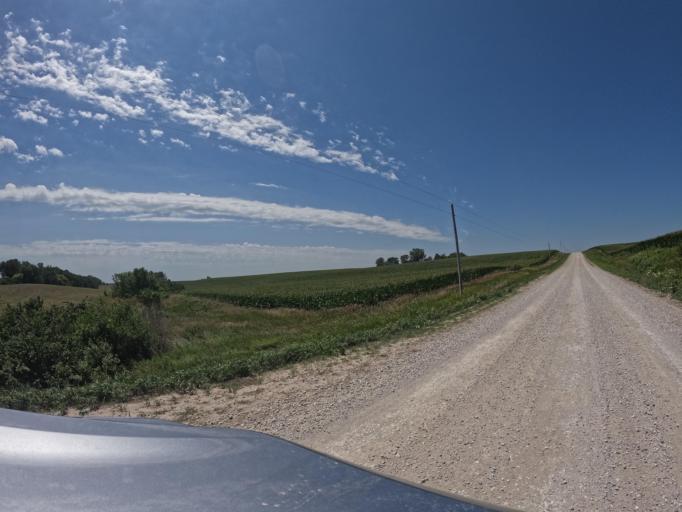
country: US
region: Iowa
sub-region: Poweshiek County
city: Montezuma
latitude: 41.4667
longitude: -92.3701
